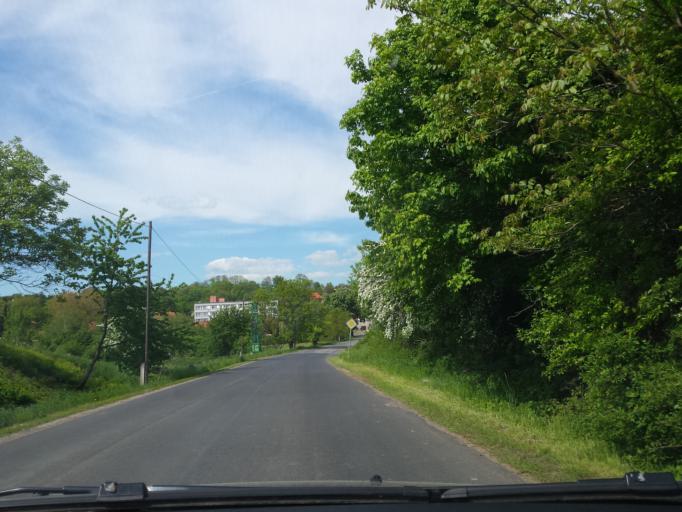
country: CZ
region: Central Bohemia
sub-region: Okres Melnik
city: Melnik
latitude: 50.4032
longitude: 14.5198
